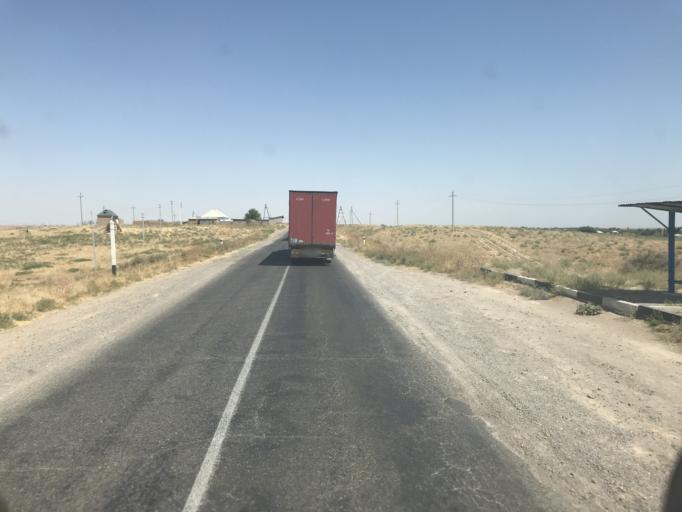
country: UZ
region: Toshkent
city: Chinoz
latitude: 41.3296
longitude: 68.6824
